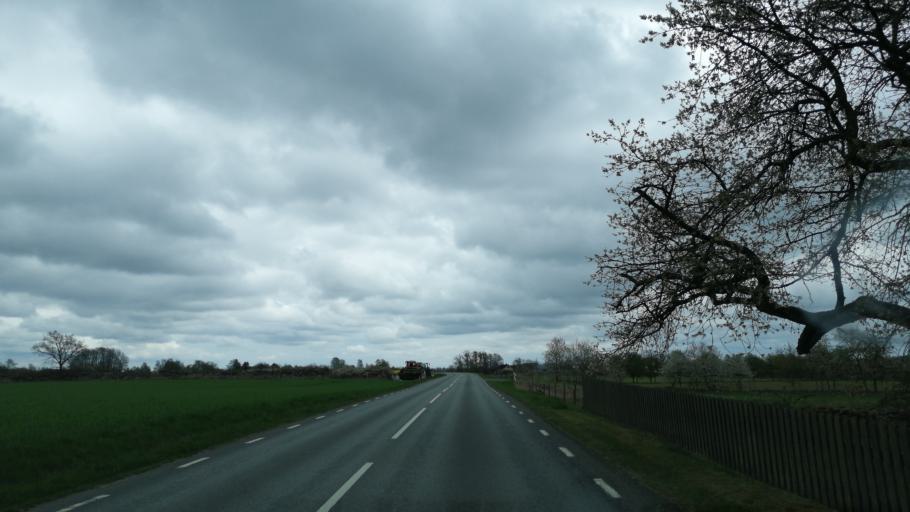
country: SE
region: Skane
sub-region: Kristianstads Kommun
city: Onnestad
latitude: 55.9936
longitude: 14.0217
